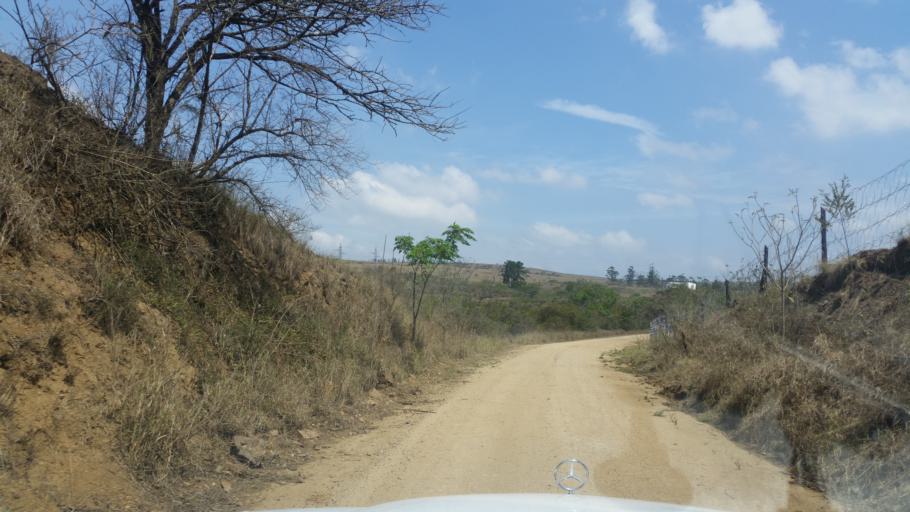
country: ZA
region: KwaZulu-Natal
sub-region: uMgungundlovu District Municipality
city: Camperdown
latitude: -29.7065
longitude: 30.4843
